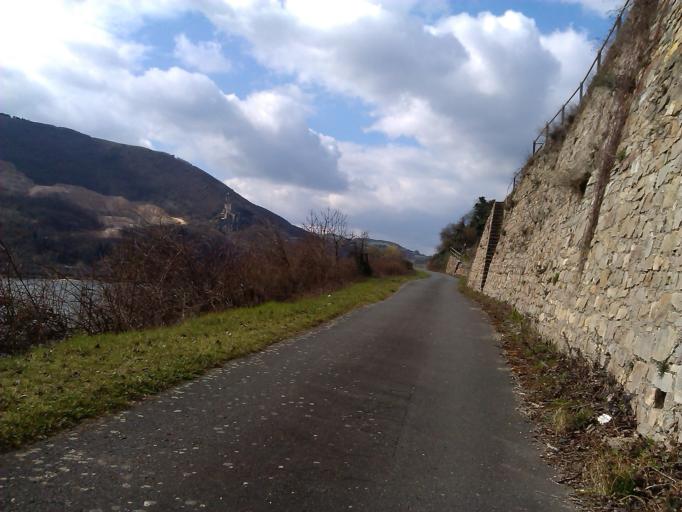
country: DE
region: Rheinland-Pfalz
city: Trechtingshausen
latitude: 50.0184
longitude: 7.8453
